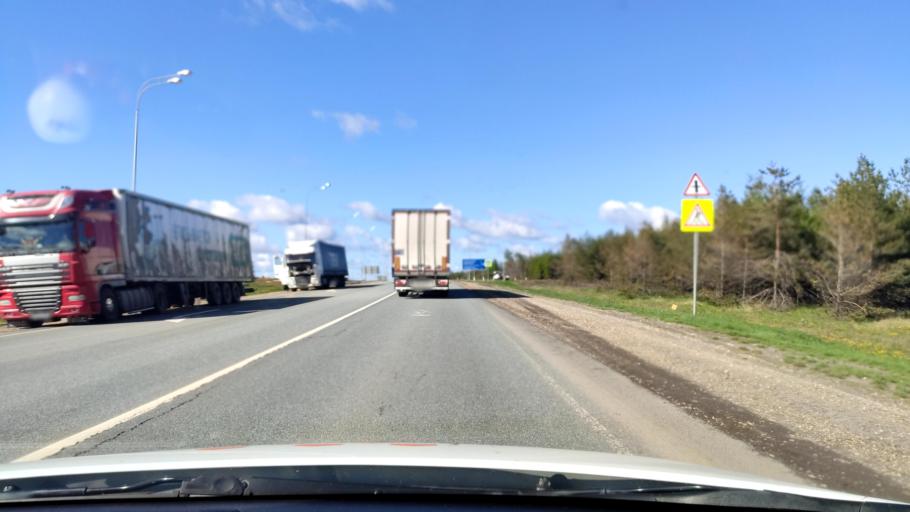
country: RU
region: Tatarstan
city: Sviyazhsk
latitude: 55.7281
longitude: 48.7622
